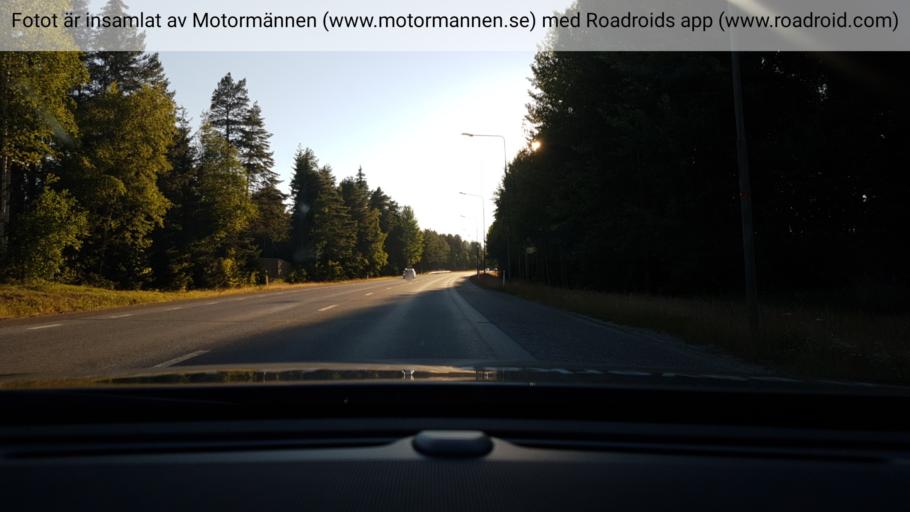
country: SE
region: Vaesterbotten
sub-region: Umea Kommun
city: Umea
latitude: 63.8361
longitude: 20.2214
